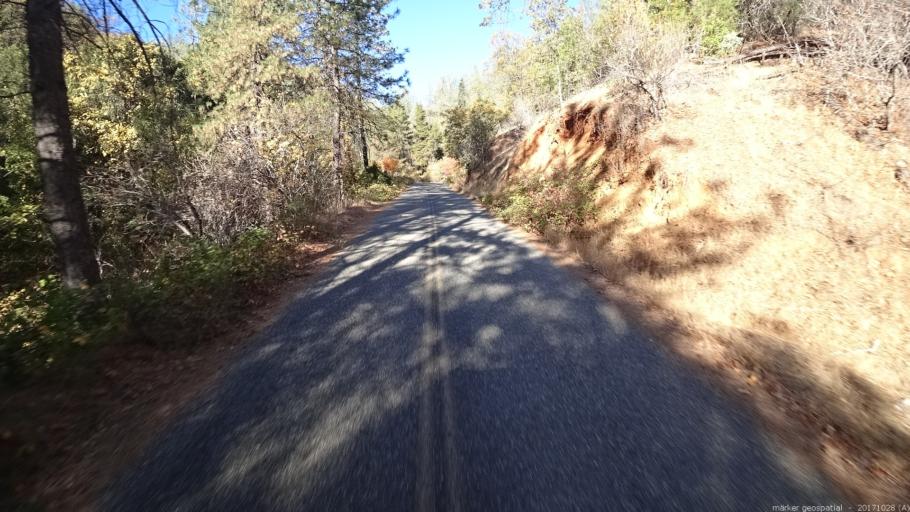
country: US
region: California
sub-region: Trinity County
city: Lewiston
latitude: 40.6506
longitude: -122.6729
